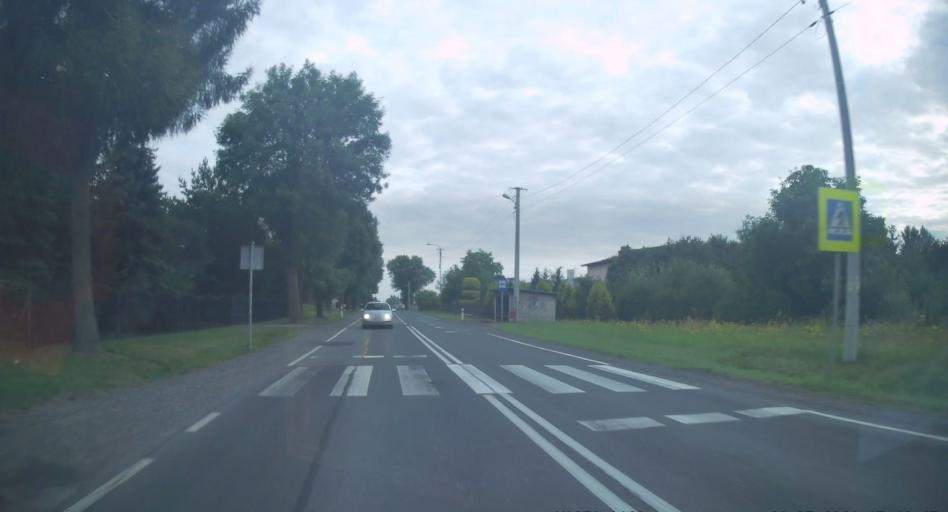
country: PL
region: Lodz Voivodeship
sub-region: Powiat radomszczanski
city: Radomsko
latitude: 51.1028
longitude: 19.4632
